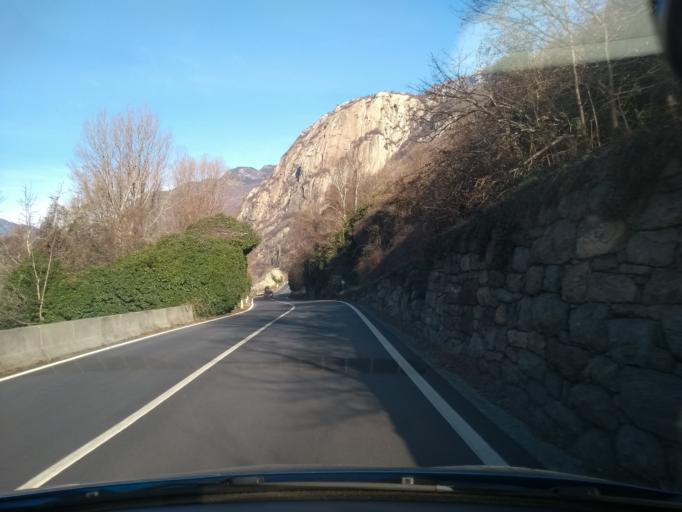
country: IT
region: Aosta Valley
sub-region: Valle d'Aosta
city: Hone
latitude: 45.6236
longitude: 7.7374
